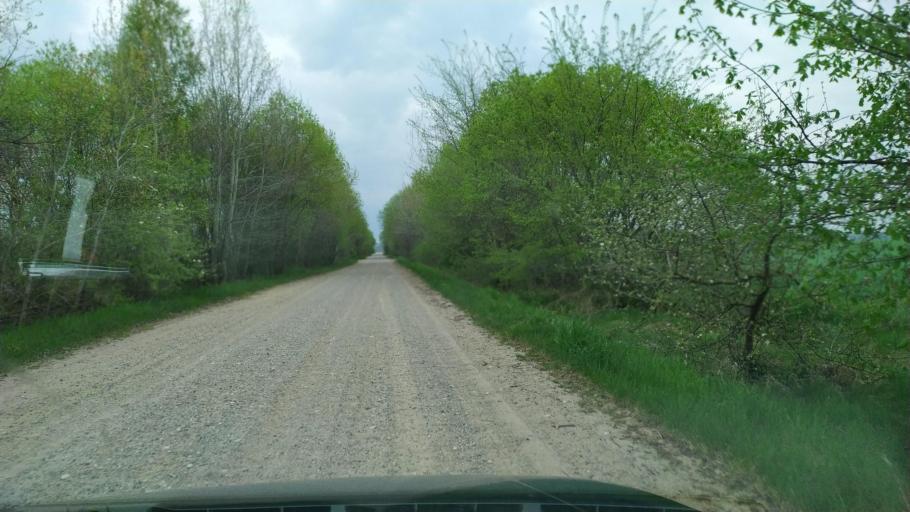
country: BY
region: Brest
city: Zhabinka
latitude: 52.1375
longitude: 24.0903
